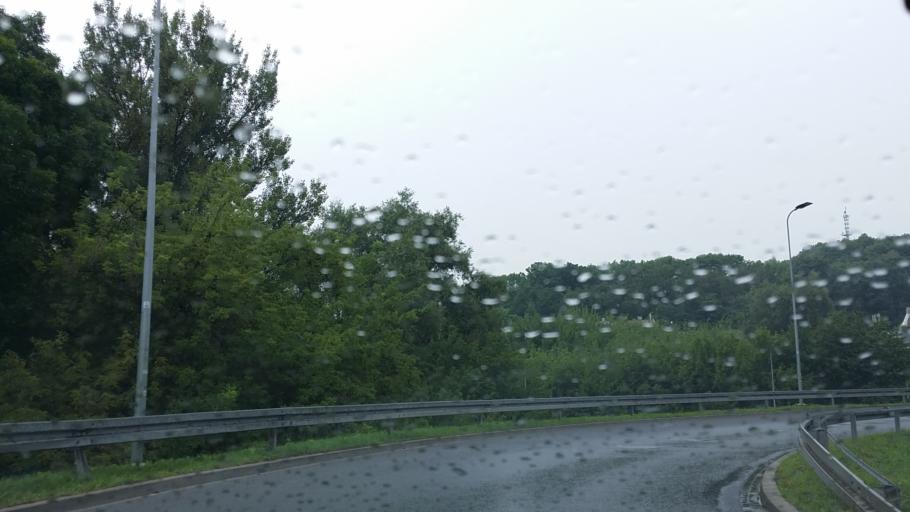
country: PL
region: Lesser Poland Voivodeship
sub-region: Krakow
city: Krakow
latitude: 50.0344
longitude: 19.9453
